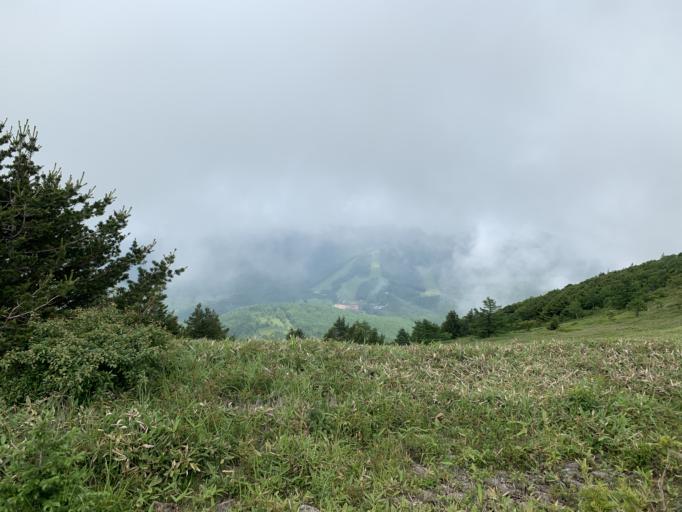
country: JP
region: Nagano
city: Ueda
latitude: 36.4366
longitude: 138.4010
